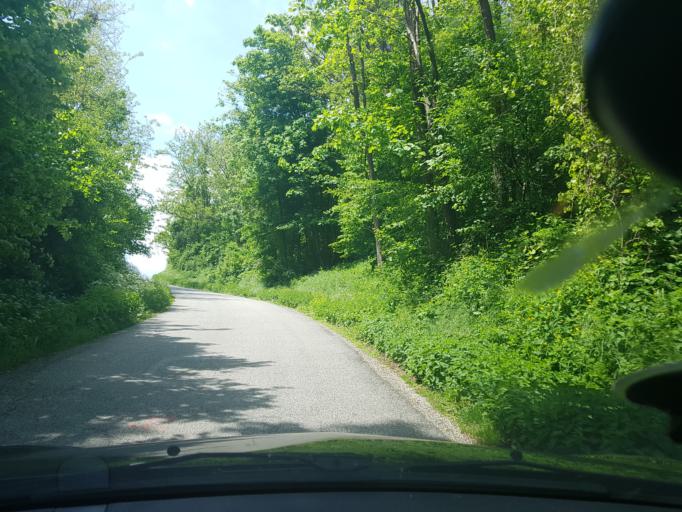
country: SI
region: Rogatec
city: Rogatec
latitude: 46.2094
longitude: 15.7203
